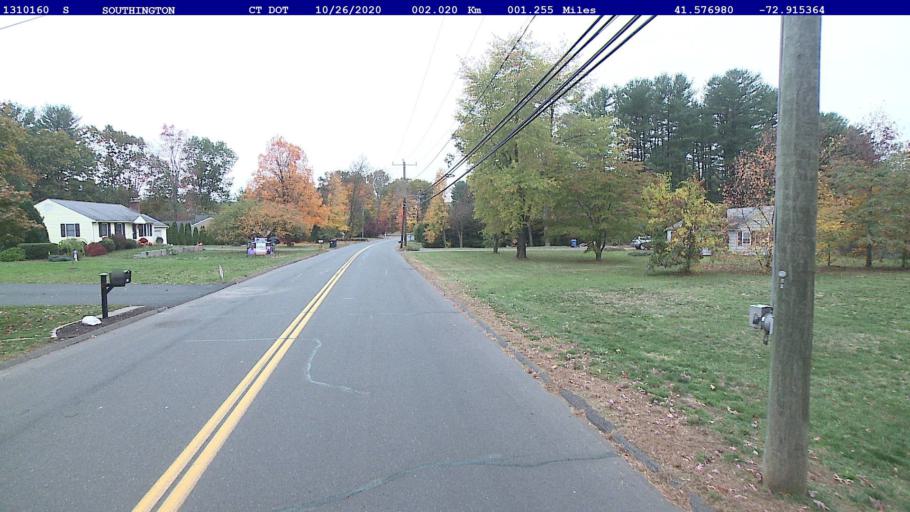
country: US
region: Connecticut
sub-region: New Haven County
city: Wolcott
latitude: 41.5770
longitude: -72.9154
